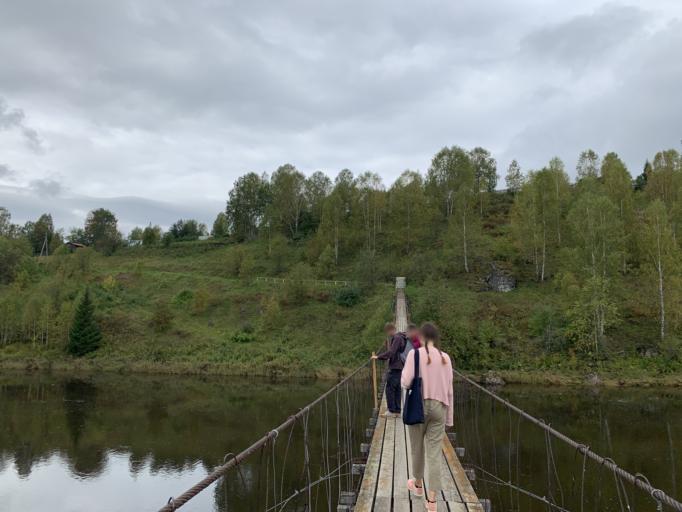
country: RU
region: Perm
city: Gubakha
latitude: 58.8632
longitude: 57.6118
